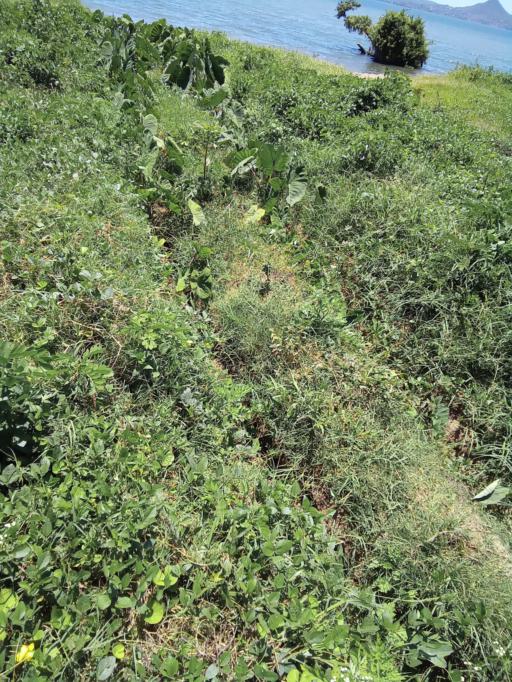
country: KE
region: Homa Bay
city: Homa Bay
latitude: -0.4742
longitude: 34.1738
